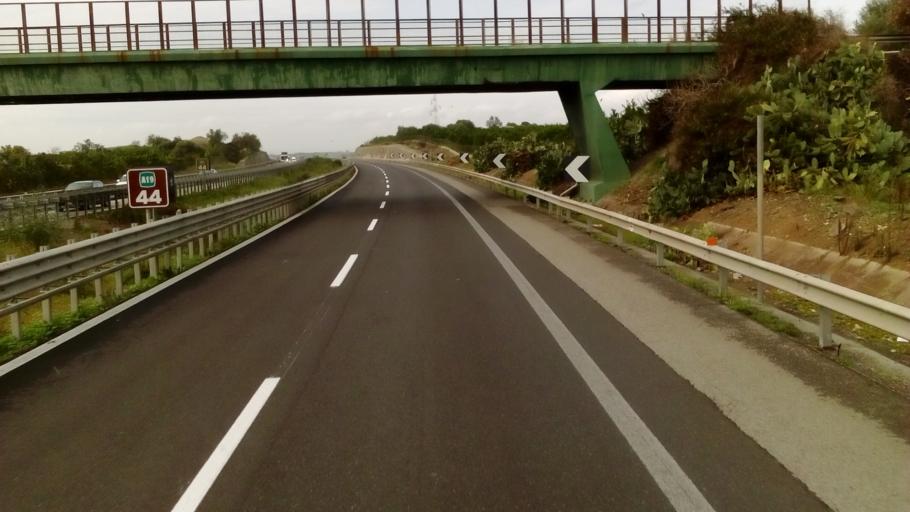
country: IT
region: Sicily
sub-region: Catania
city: Motta Sant'Anastasia
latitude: 37.4681
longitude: 14.9054
